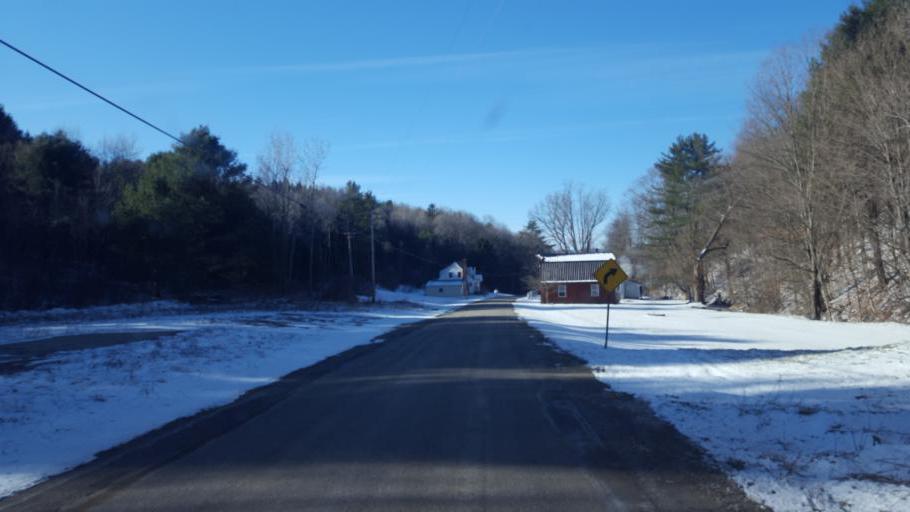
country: US
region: New York
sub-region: Allegany County
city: Wellsville
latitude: 42.1417
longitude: -77.9092
